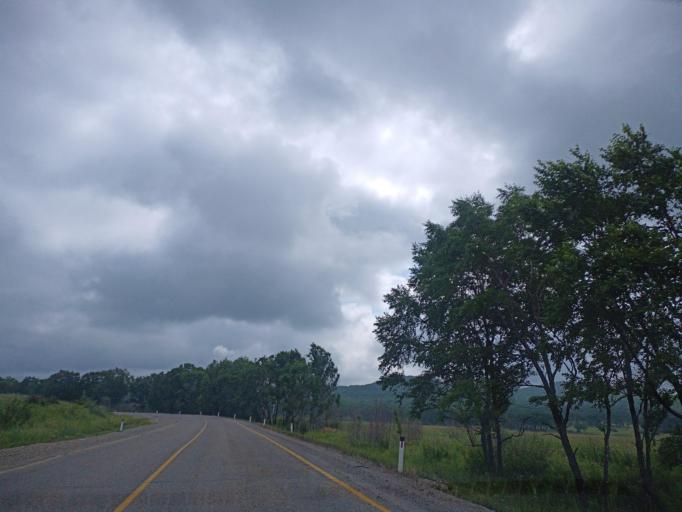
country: RU
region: Primorskiy
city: Dal'nerechensk
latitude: 46.0379
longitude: 133.8869
